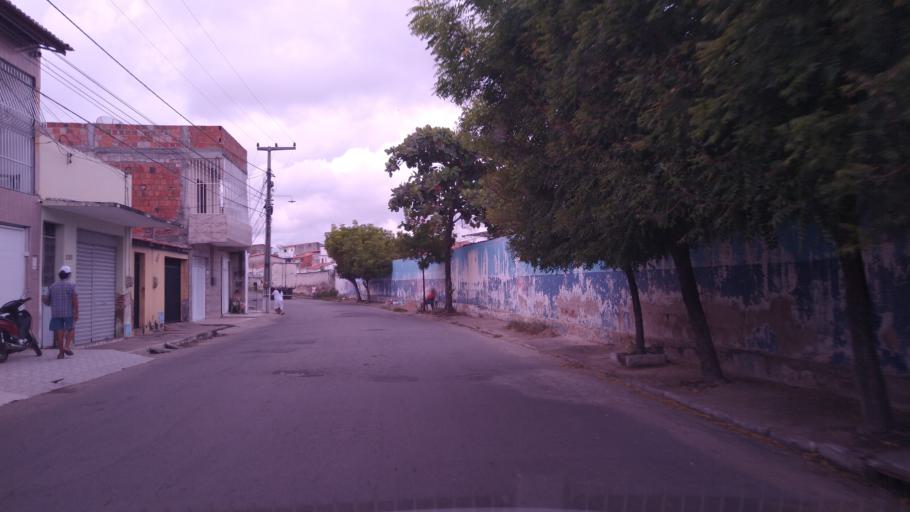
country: BR
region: Ceara
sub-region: Quixada
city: Quixada
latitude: -4.9640
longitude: -39.0143
